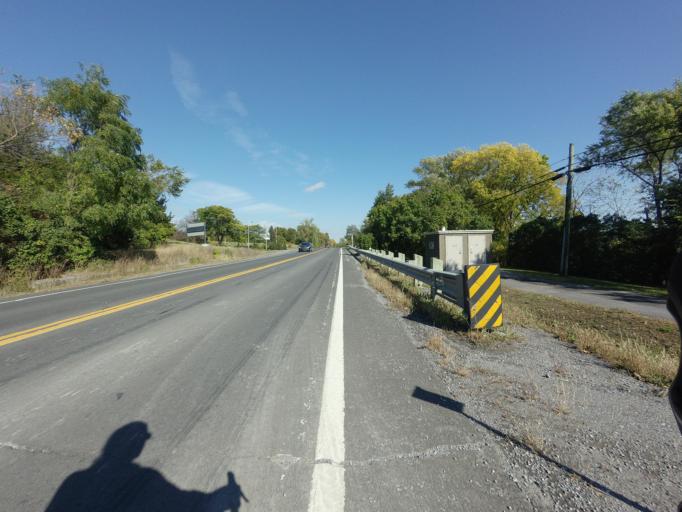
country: CA
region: Ontario
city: Skatepark
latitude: 44.1871
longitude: -76.7508
